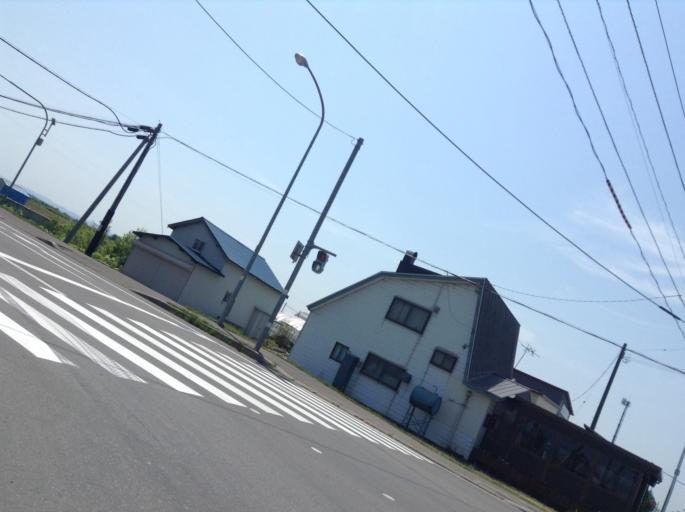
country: JP
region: Hokkaido
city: Nayoro
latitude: 44.3616
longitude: 142.4363
